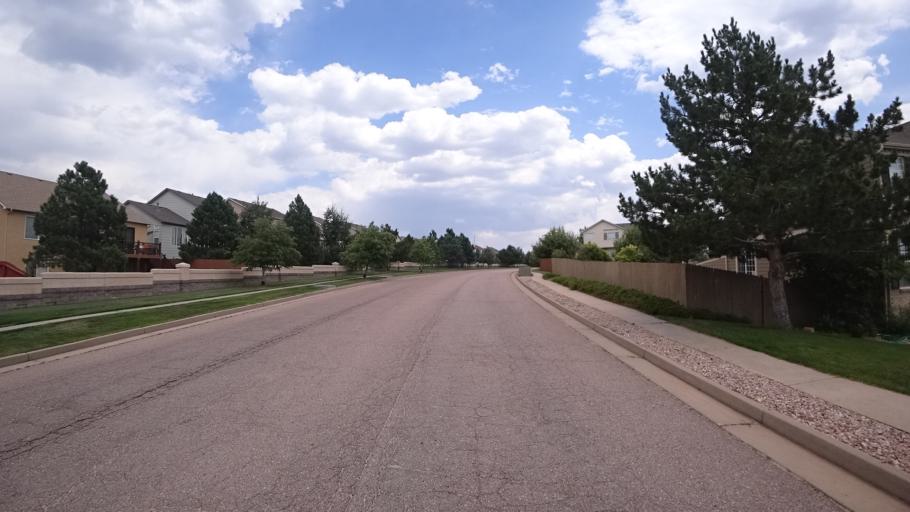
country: US
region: Colorado
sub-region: El Paso County
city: Black Forest
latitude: 38.9638
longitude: -104.7429
